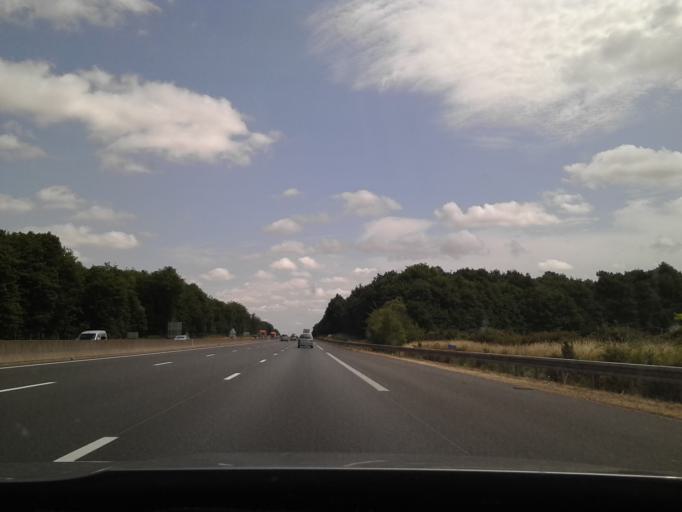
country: FR
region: Centre
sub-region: Departement d'Indre-et-Loire
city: Monnaie
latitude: 47.4923
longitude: 0.8279
